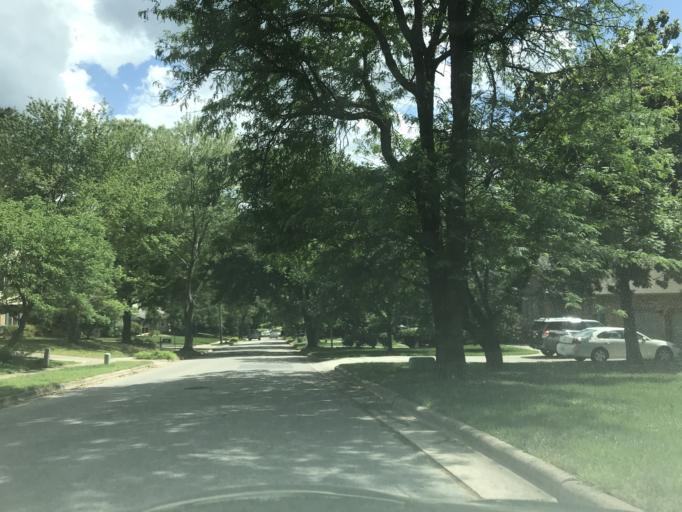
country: US
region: North Carolina
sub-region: Wake County
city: West Raleigh
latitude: 35.8560
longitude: -78.6294
